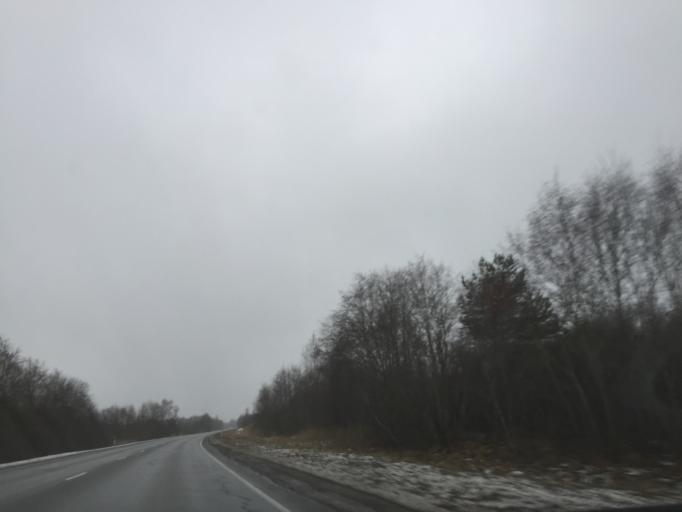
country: EE
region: Laeaene
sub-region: Lihula vald
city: Lihula
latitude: 58.5988
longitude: 23.5515
